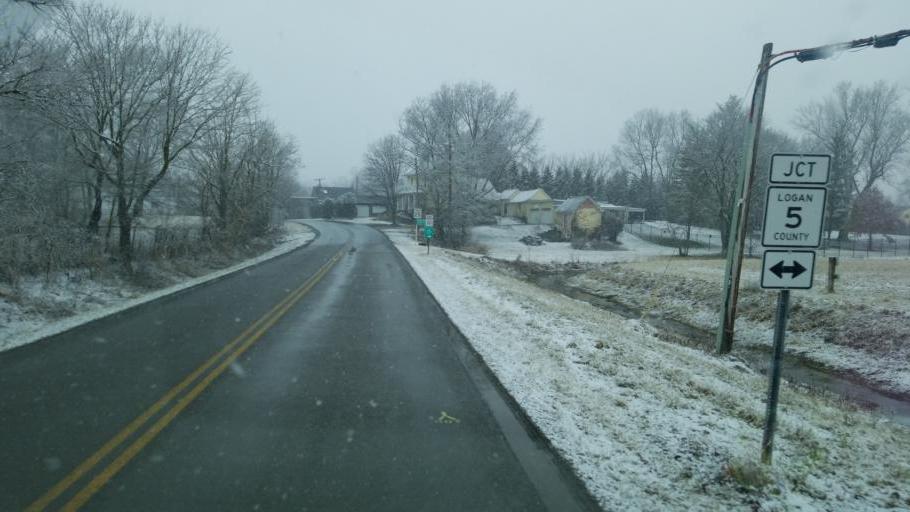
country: US
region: Ohio
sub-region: Logan County
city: Bellefontaine
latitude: 40.3366
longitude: -83.6756
